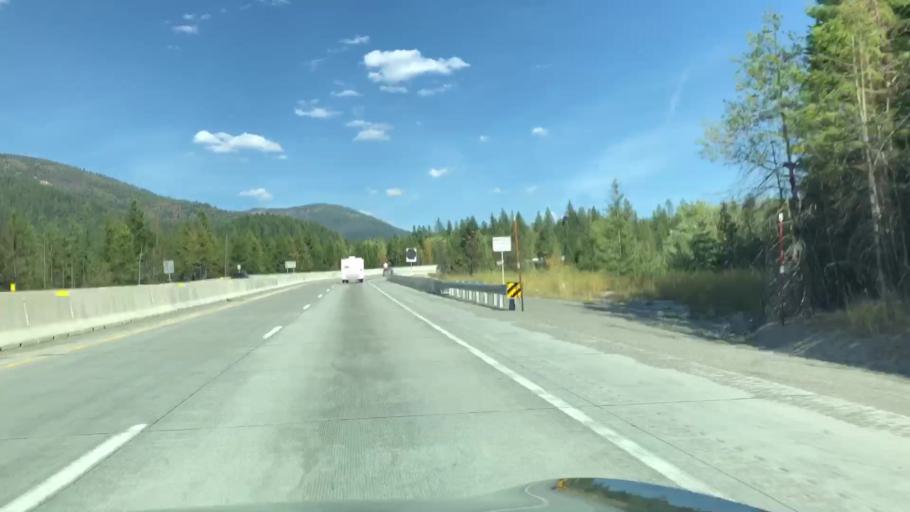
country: US
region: Idaho
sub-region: Shoshone County
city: Wallace
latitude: 47.4696
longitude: -115.7678
